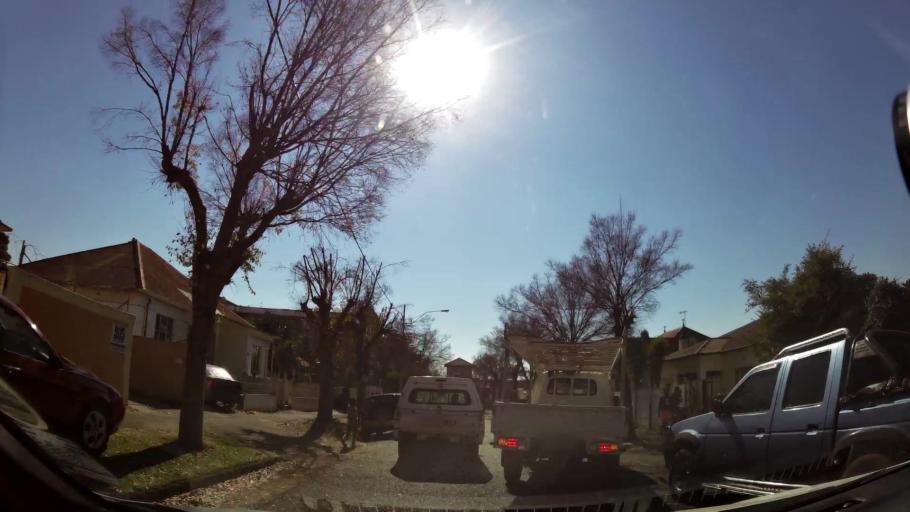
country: ZA
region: Gauteng
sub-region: City of Johannesburg Metropolitan Municipality
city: Johannesburg
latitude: -26.2458
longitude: 28.0544
